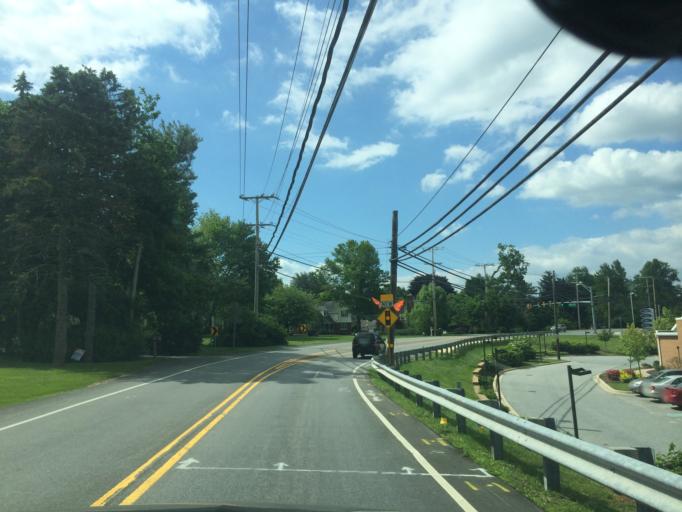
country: US
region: Maryland
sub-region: Carroll County
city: Westminster
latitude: 39.5599
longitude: -76.9868
